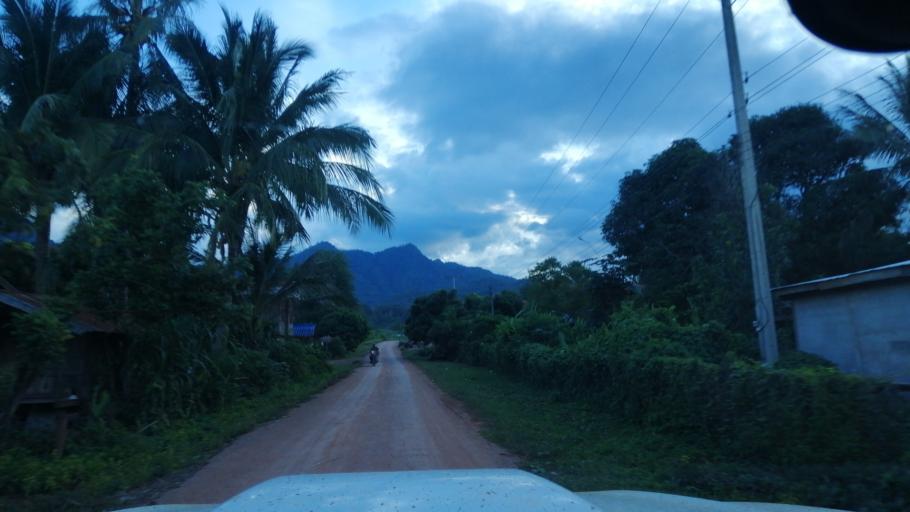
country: TH
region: Uttaradit
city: Ban Khok
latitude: 17.8704
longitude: 101.0911
